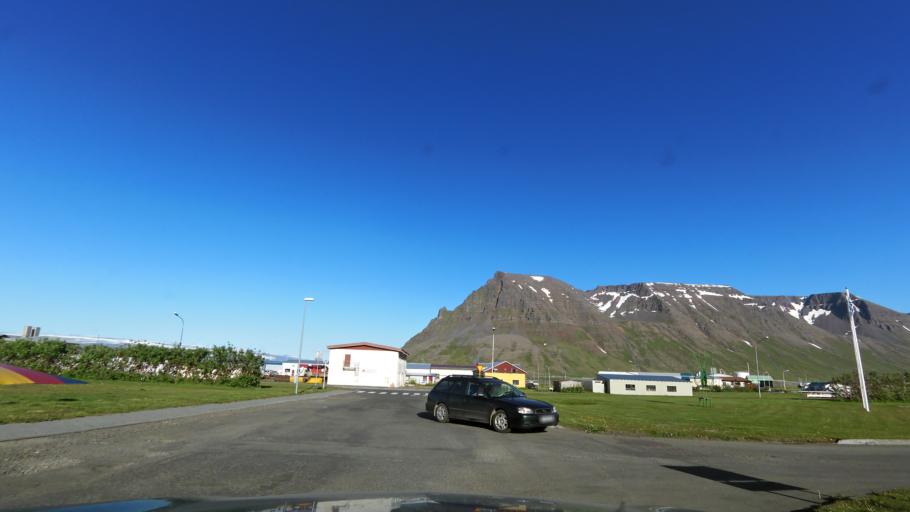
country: IS
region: Westfjords
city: Isafjoerdur
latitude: 66.1562
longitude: -23.2527
